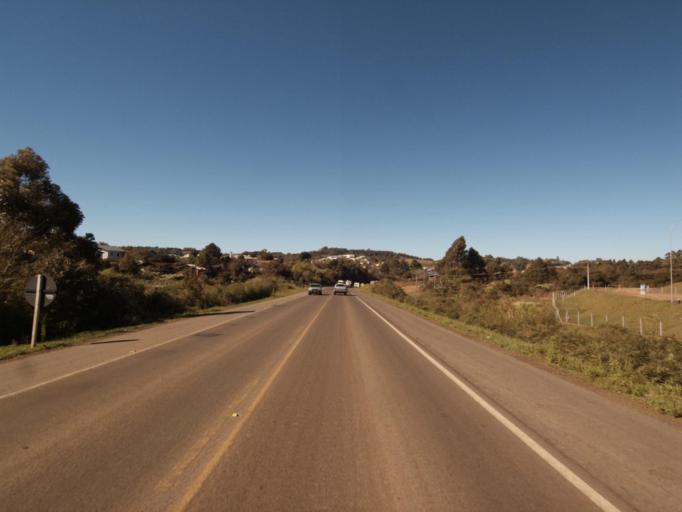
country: BR
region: Santa Catarina
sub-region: Sao Lourenco Do Oeste
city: Sao Lourenco dOeste
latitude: -26.7769
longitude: -53.2006
